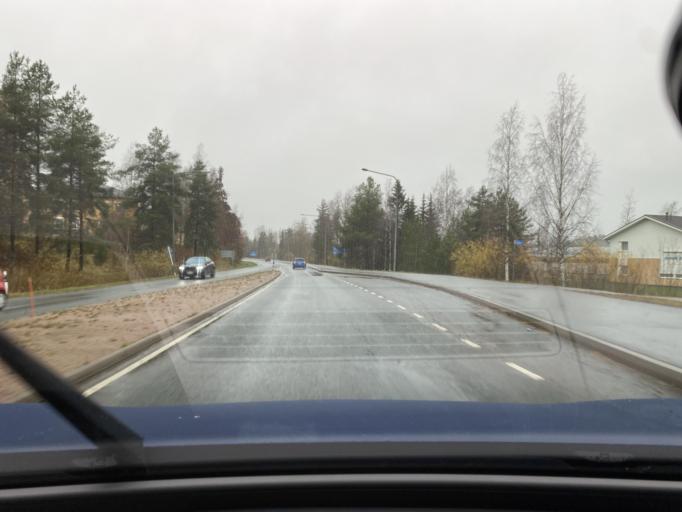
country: FI
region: Varsinais-Suomi
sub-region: Loimaa
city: Loimaa
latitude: 60.8569
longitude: 23.0363
